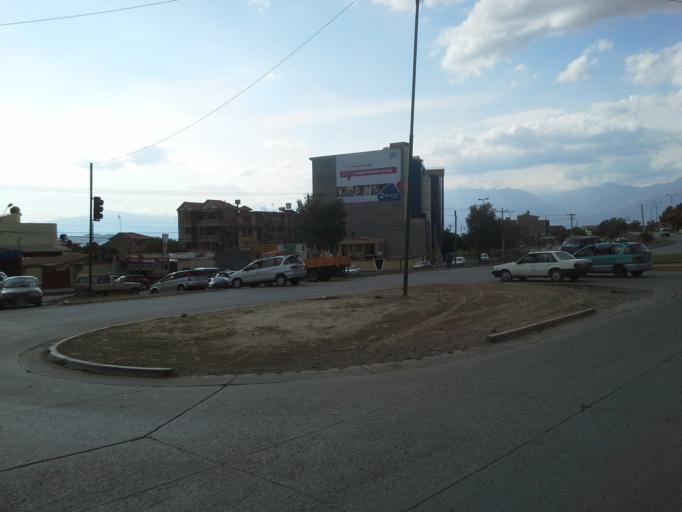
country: BO
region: Cochabamba
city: Cochabamba
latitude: -17.4300
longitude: -66.1510
